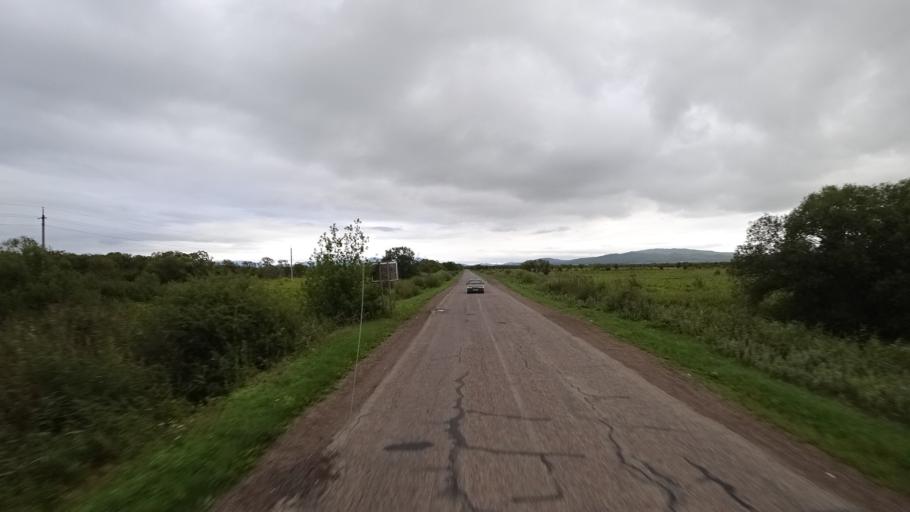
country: RU
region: Primorskiy
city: Chernigovka
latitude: 44.3627
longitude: 132.5529
